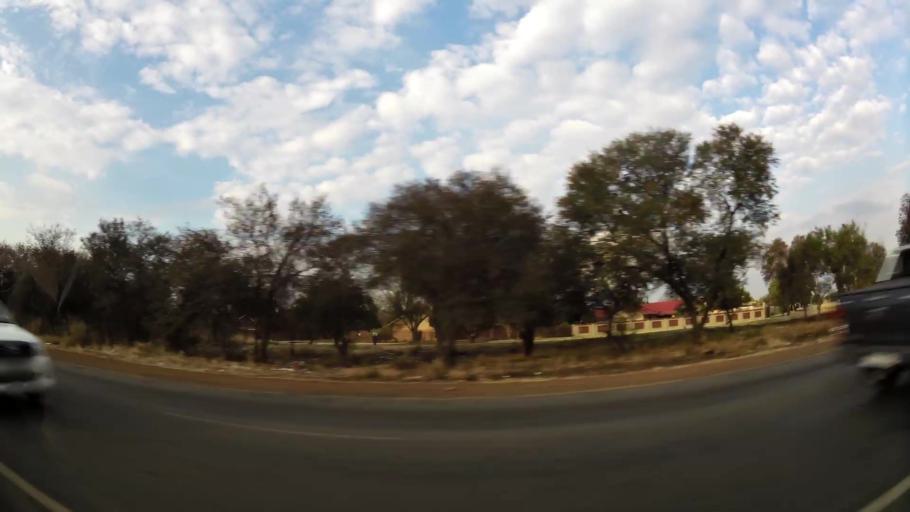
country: ZA
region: Gauteng
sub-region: Sedibeng District Municipality
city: Vanderbijlpark
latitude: -26.7158
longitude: 27.8181
